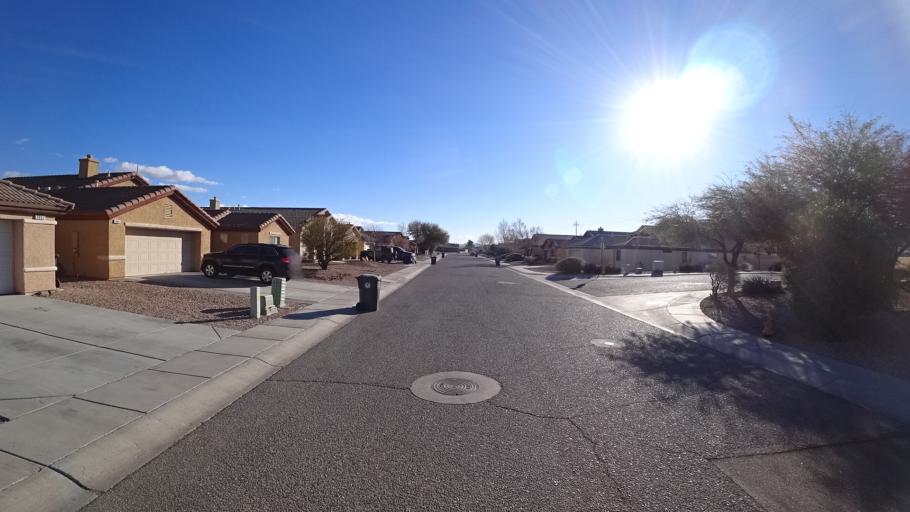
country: US
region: Arizona
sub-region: Mohave County
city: New Kingman-Butler
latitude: 35.2254
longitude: -113.9791
